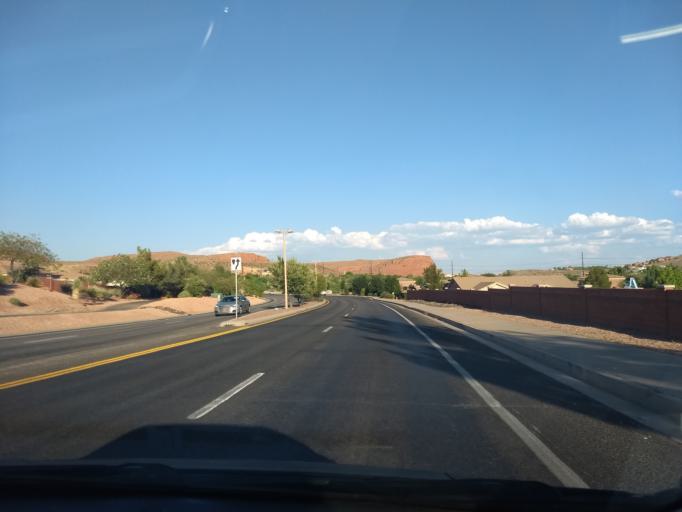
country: US
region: Utah
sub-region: Washington County
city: Santa Clara
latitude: 37.1343
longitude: -113.6150
